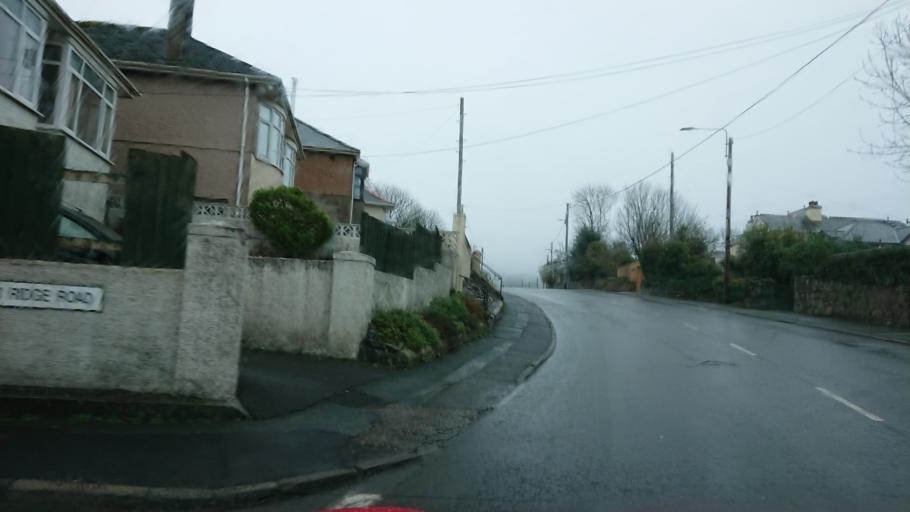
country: GB
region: England
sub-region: Plymouth
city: Plymstock
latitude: 50.3571
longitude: -4.0990
